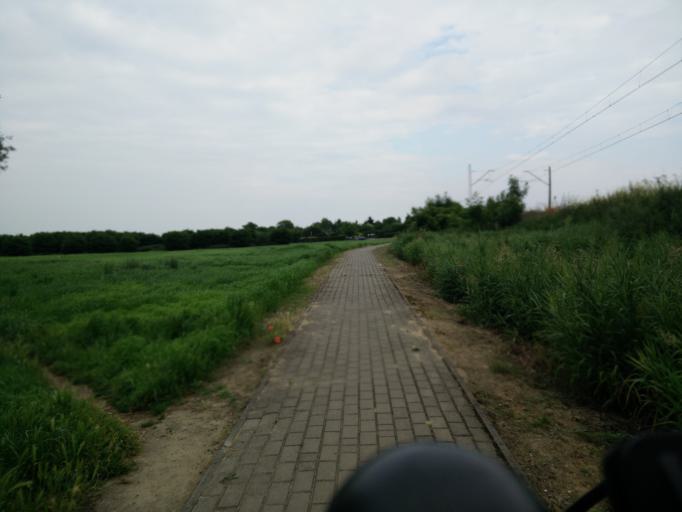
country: PL
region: Greater Poland Voivodeship
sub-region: Powiat sredzki
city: Sroda Wielkopolska
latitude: 52.2156
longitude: 17.2805
